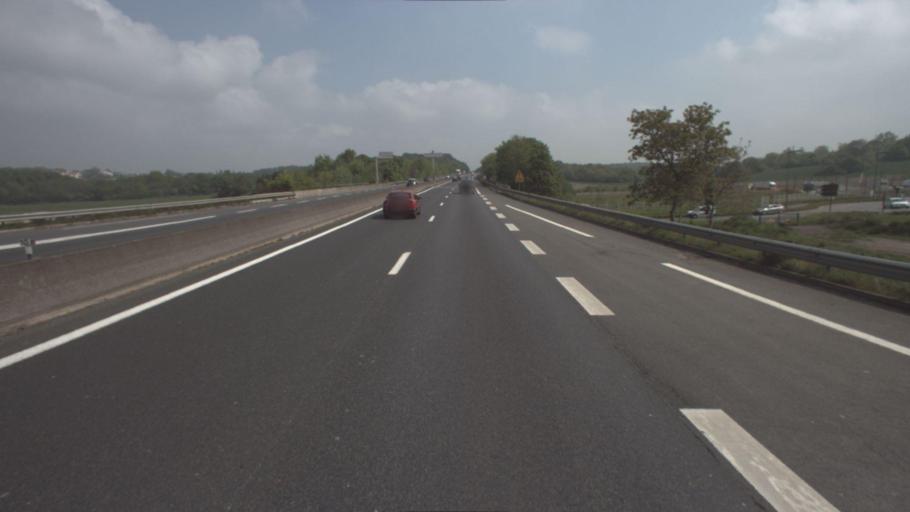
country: FR
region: Ile-de-France
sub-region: Departement de Seine-et-Marne
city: Saint-Mard
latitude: 49.0398
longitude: 2.6834
